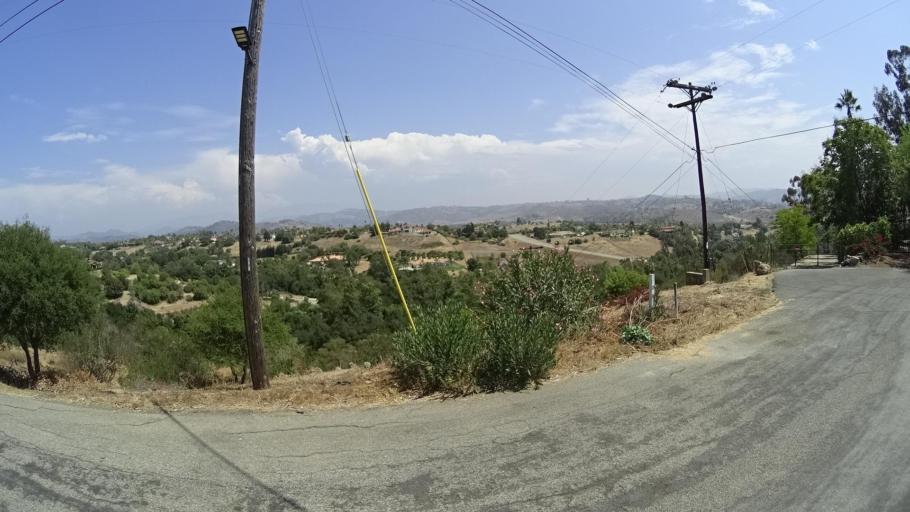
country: US
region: California
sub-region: San Diego County
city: Bonsall
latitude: 33.3089
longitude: -117.2236
